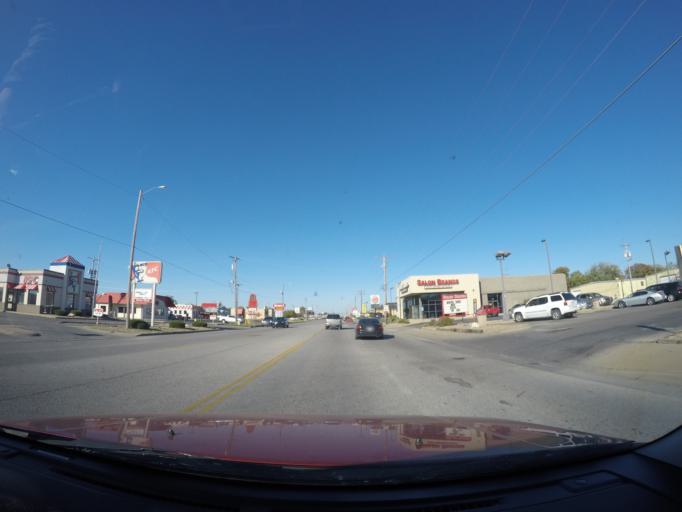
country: US
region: Kansas
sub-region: Sedgwick County
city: Wichita
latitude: 37.6770
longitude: -97.3893
